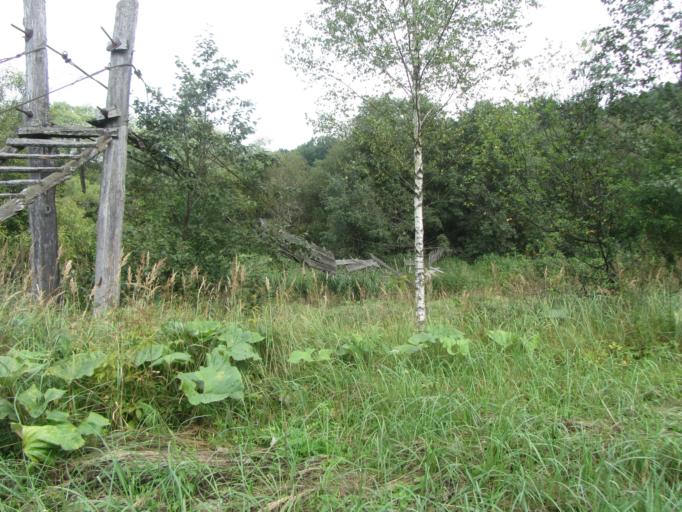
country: LT
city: Silale
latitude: 55.3554
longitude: 22.1936
